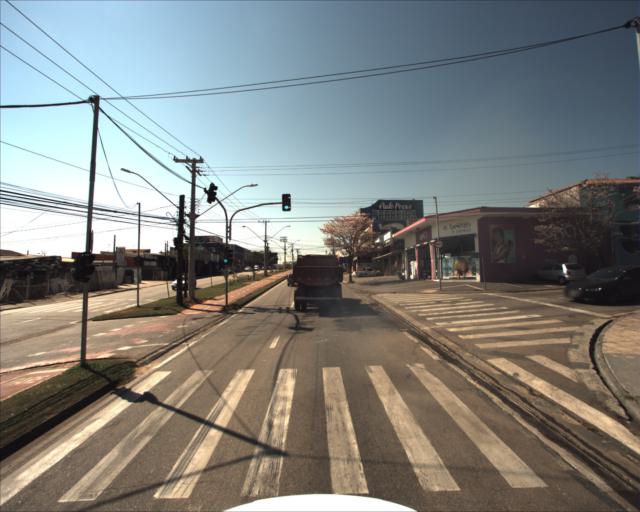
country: BR
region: Sao Paulo
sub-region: Sorocaba
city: Sorocaba
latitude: -23.5031
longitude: -47.5207
